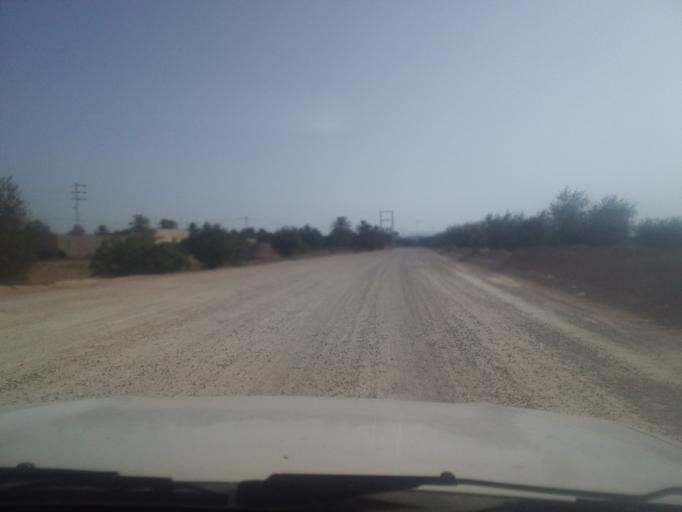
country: TN
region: Qabis
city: Matmata
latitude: 33.6027
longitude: 10.2771
